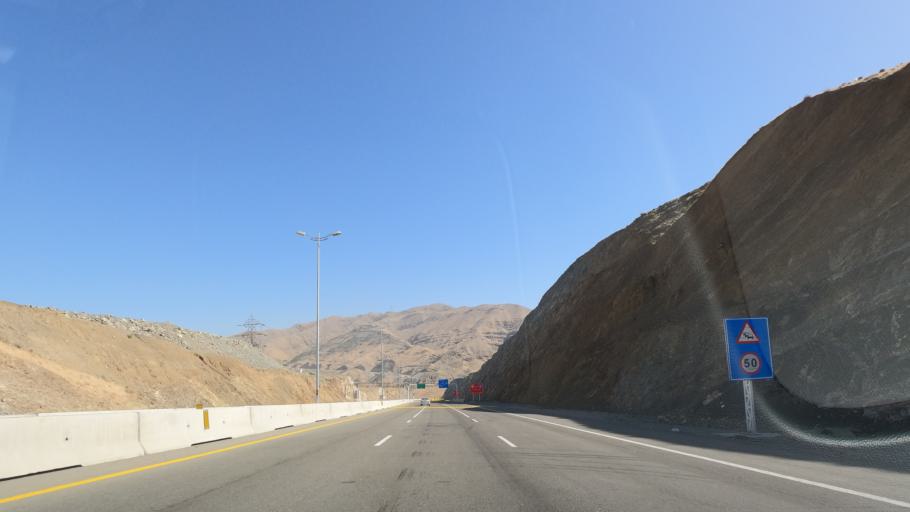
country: IR
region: Alborz
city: Karaj
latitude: 35.8174
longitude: 51.0379
